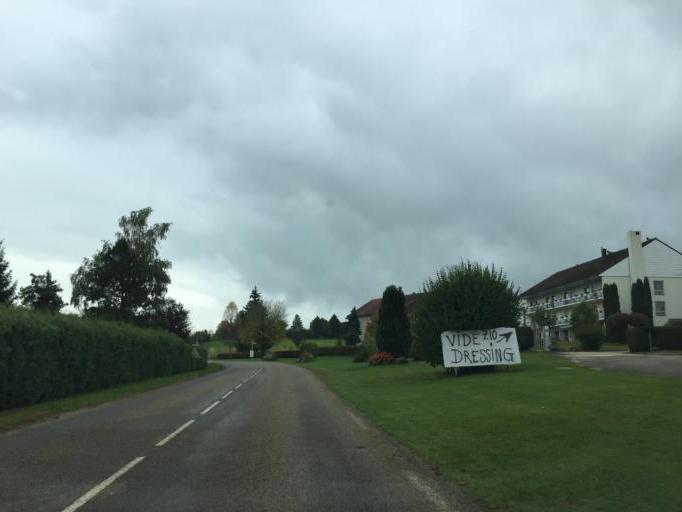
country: FR
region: Franche-Comte
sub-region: Departement du Jura
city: Orgelet
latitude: 46.5155
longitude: 5.6071
